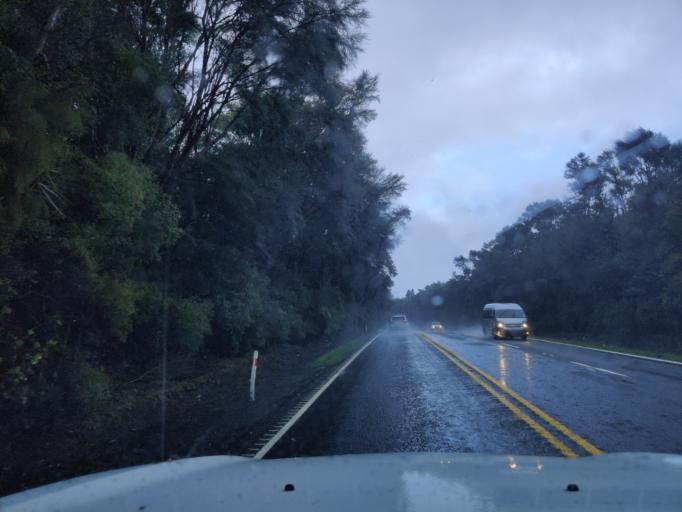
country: NZ
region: Waikato
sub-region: South Waikato District
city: Tokoroa
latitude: -38.0207
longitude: 175.9561
